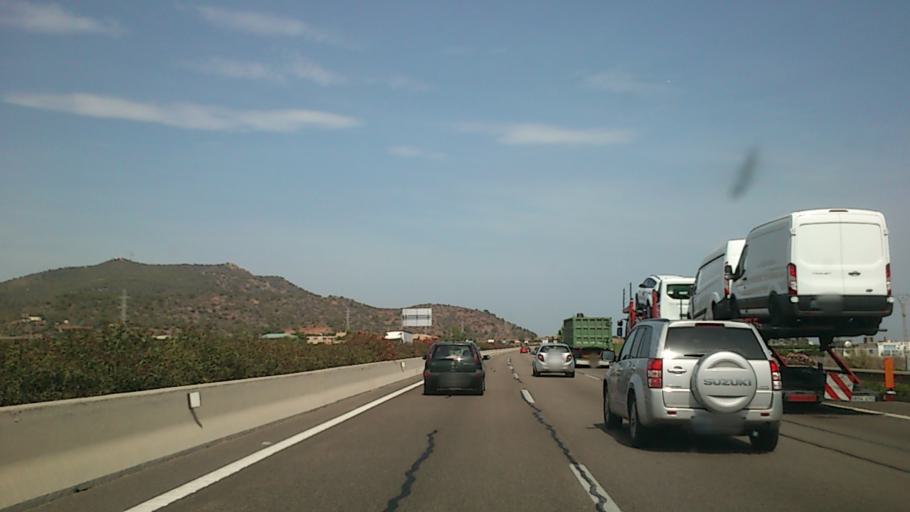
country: ES
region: Valencia
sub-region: Provincia de Valencia
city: Pucol
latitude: 39.6174
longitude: -0.3363
